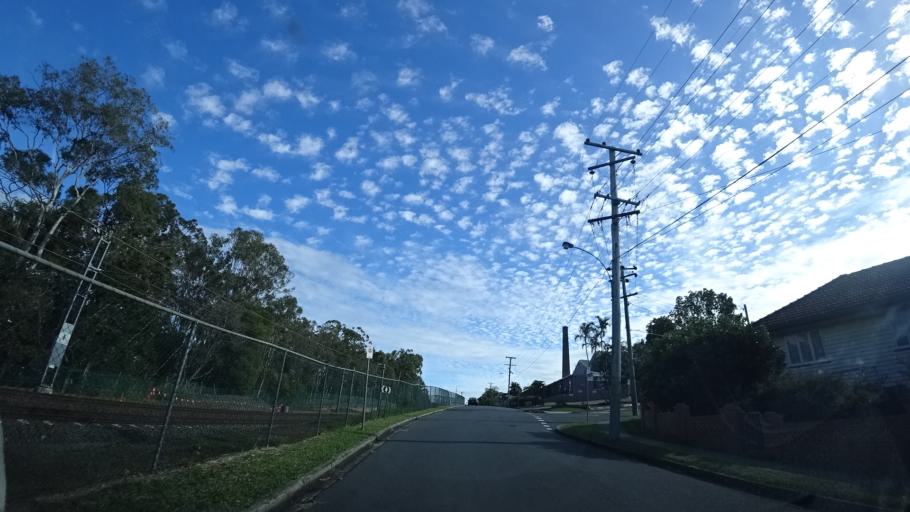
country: AU
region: Queensland
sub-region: Brisbane
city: Grange
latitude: -27.4291
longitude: 153.0077
